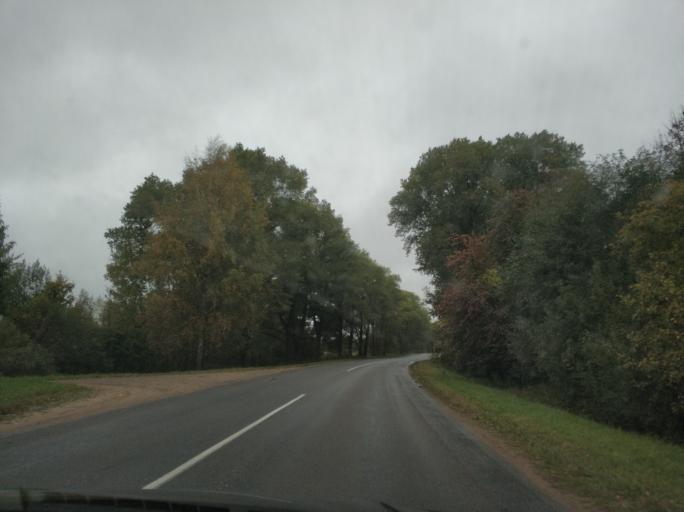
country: BY
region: Vitebsk
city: Polatsk
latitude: 55.4450
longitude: 28.9430
